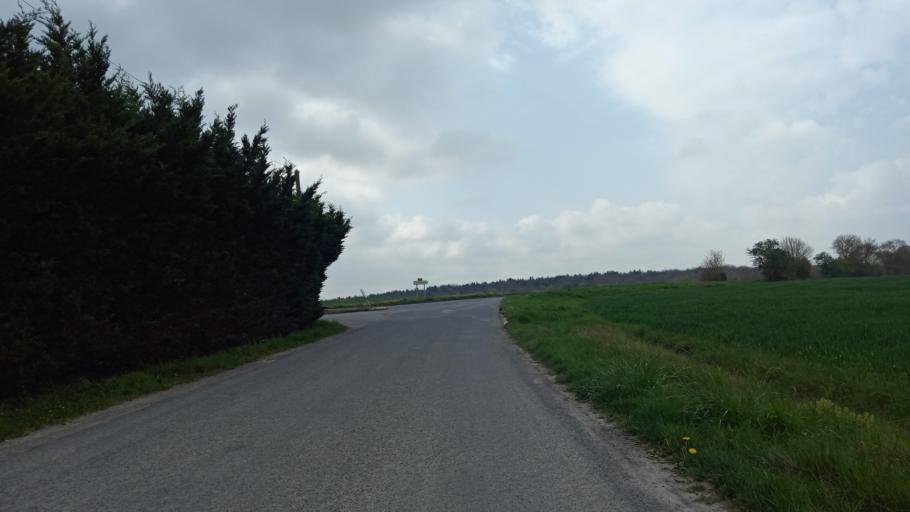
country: FR
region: Poitou-Charentes
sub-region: Departement de la Charente-Maritime
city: Verines
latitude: 46.1520
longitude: -0.9324
